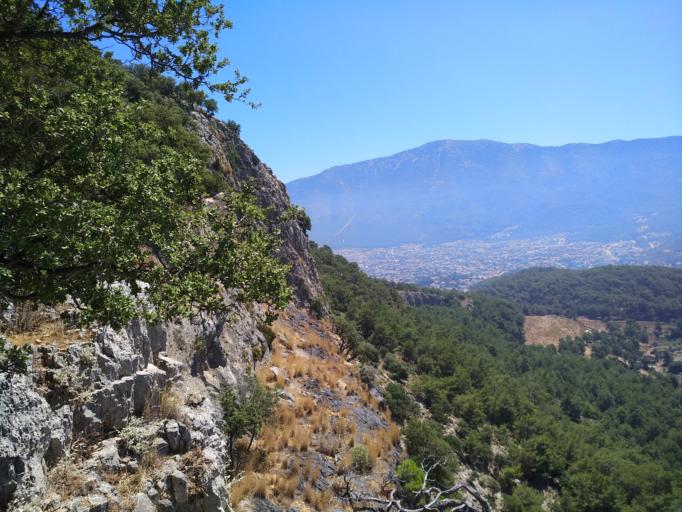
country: TR
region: Mugla
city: OEluedeniz
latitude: 36.5671
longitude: 29.1133
